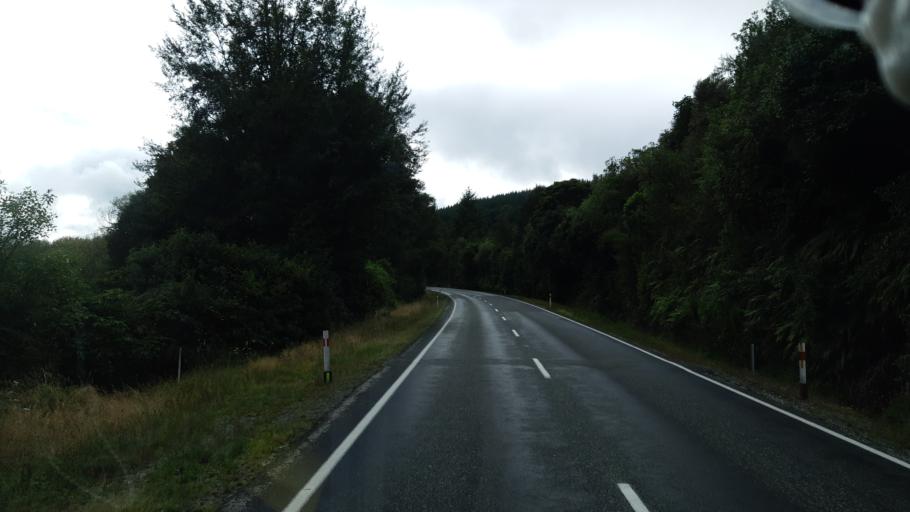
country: NZ
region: West Coast
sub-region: Buller District
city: Westport
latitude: -41.9195
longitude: 172.2210
